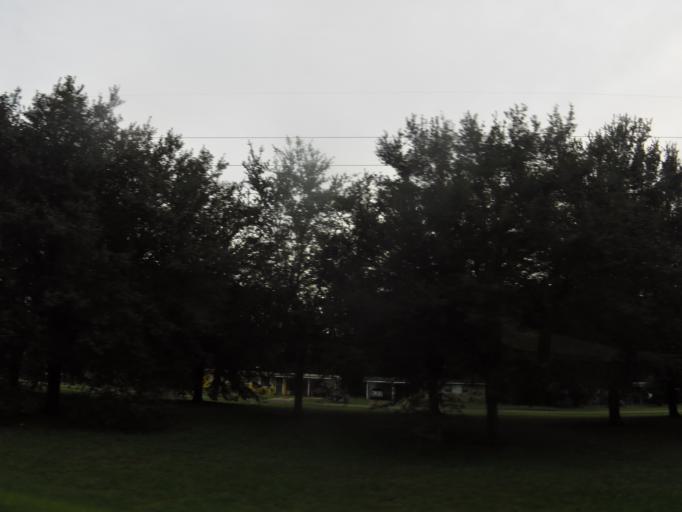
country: US
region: Florida
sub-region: Duval County
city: Jacksonville
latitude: 30.3515
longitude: -81.7216
